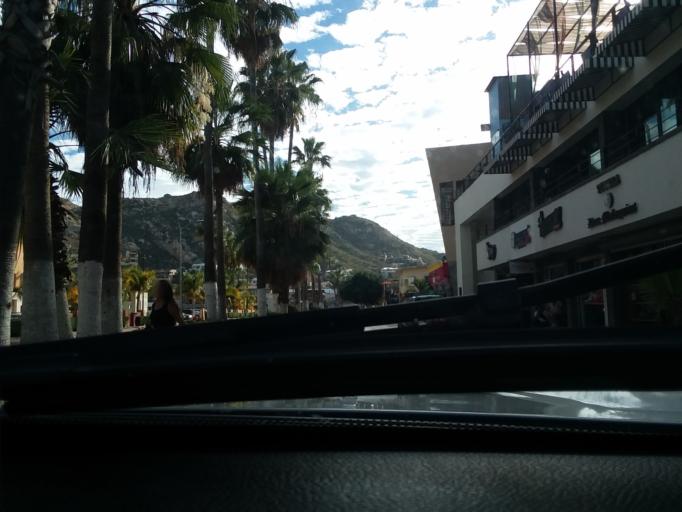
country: MX
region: Baja California Sur
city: Cabo San Lucas
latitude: 22.8815
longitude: -109.9124
